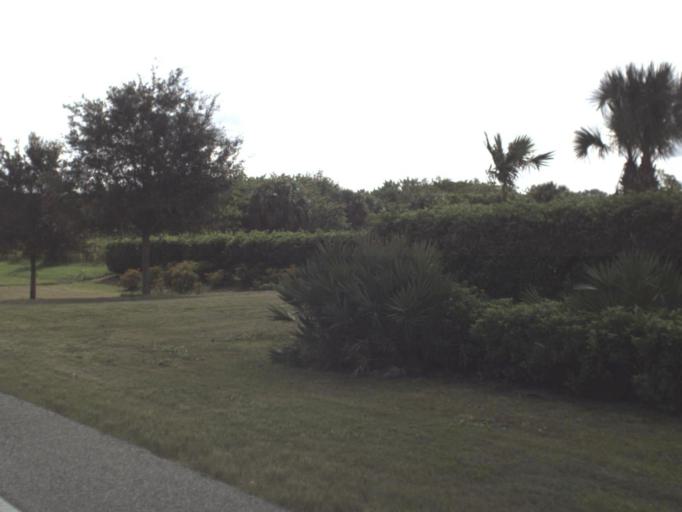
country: US
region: Florida
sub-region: Lee County
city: Alva
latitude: 26.7094
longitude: -81.5659
